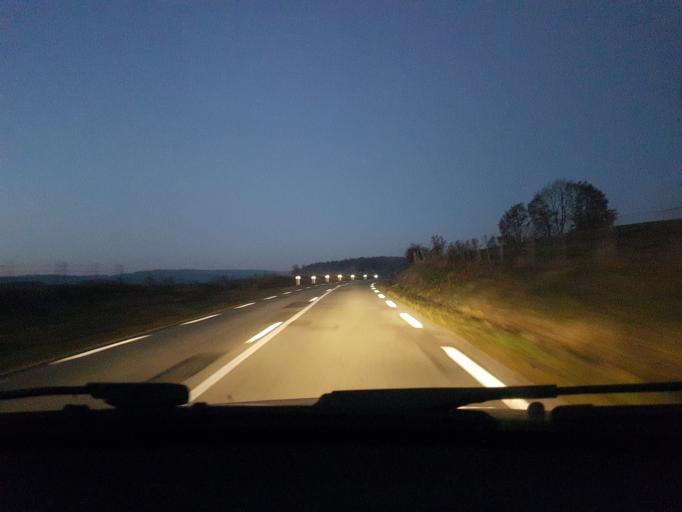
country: FR
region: Franche-Comte
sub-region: Departement du Doubs
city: Les Fins
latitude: 47.0930
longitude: 6.6479
